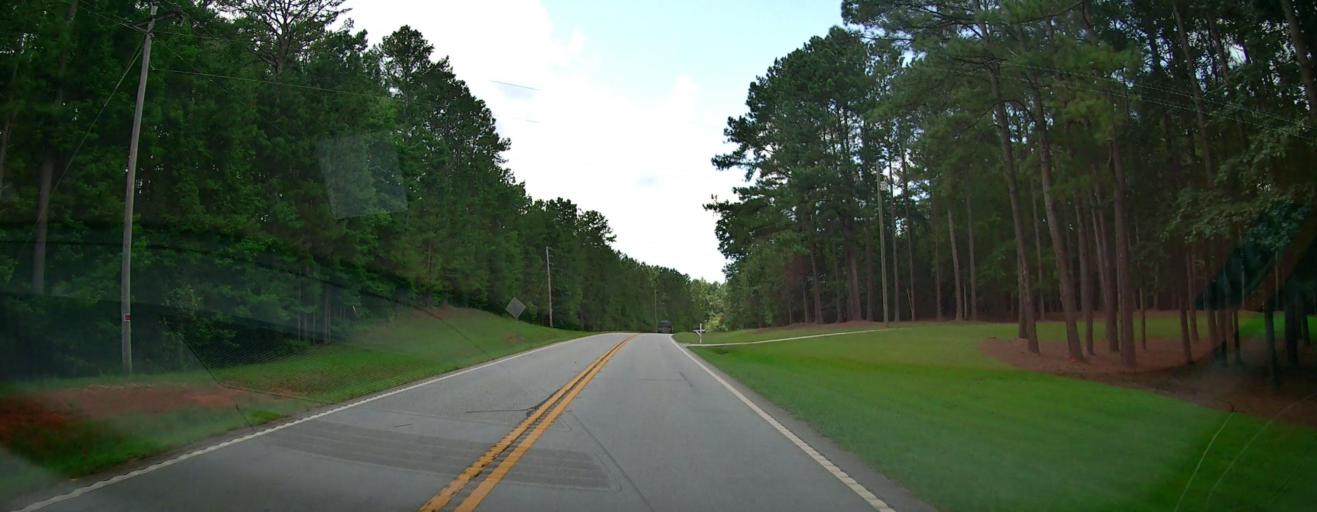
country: US
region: Georgia
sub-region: Heard County
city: Franklin
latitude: 33.3158
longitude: -85.1525
